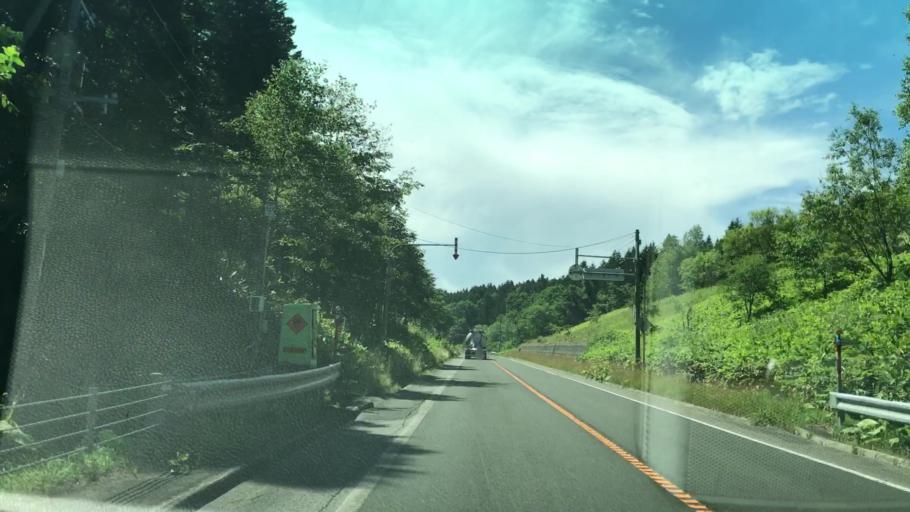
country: JP
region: Hokkaido
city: Shimo-furano
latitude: 42.9182
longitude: 142.4474
